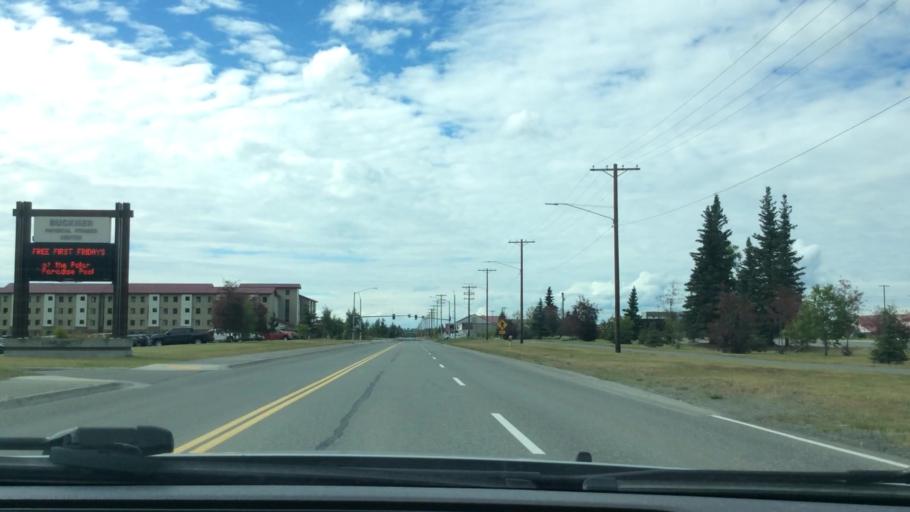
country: US
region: Alaska
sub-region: Anchorage Municipality
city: Elmendorf Air Force Base
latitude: 61.2588
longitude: -149.6795
